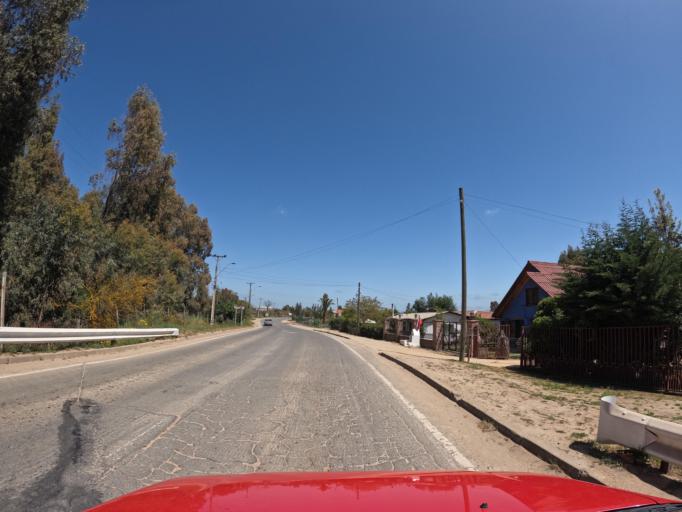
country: CL
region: O'Higgins
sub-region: Provincia de Colchagua
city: Santa Cruz
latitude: -34.7282
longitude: -71.6651
